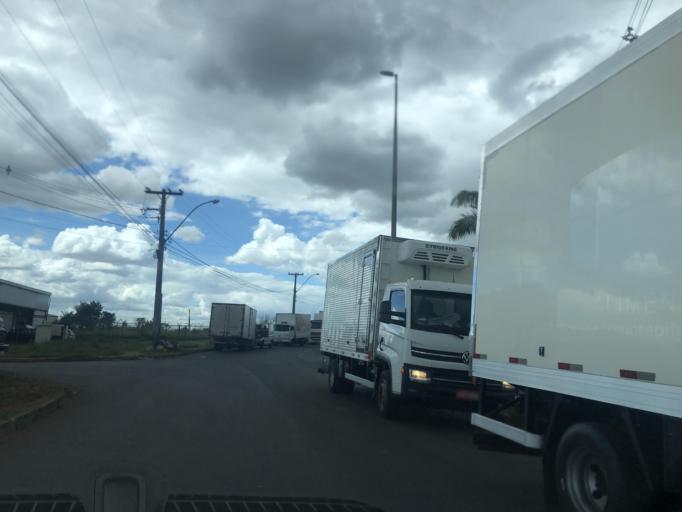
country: BR
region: Federal District
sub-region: Brasilia
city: Brasilia
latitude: -15.8740
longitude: -48.0268
